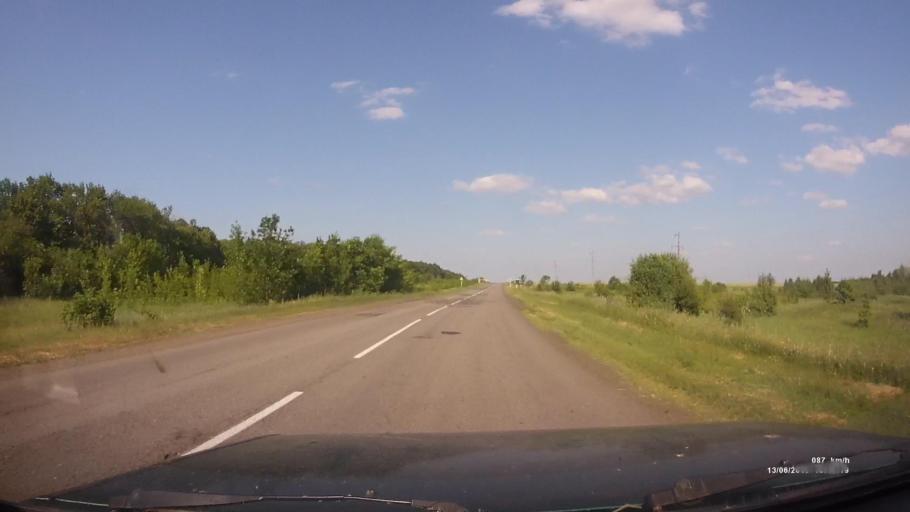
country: RU
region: Rostov
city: Kazanskaya
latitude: 49.9271
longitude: 41.3377
